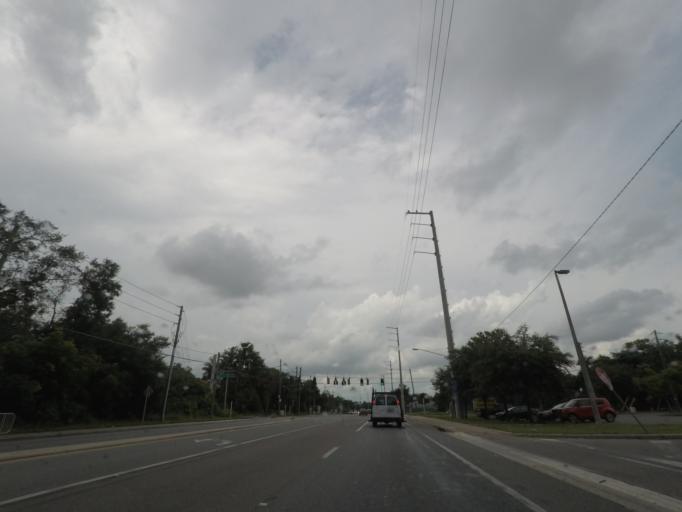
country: US
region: Florida
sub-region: Polk County
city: Loughman
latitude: 28.2416
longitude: -81.5663
